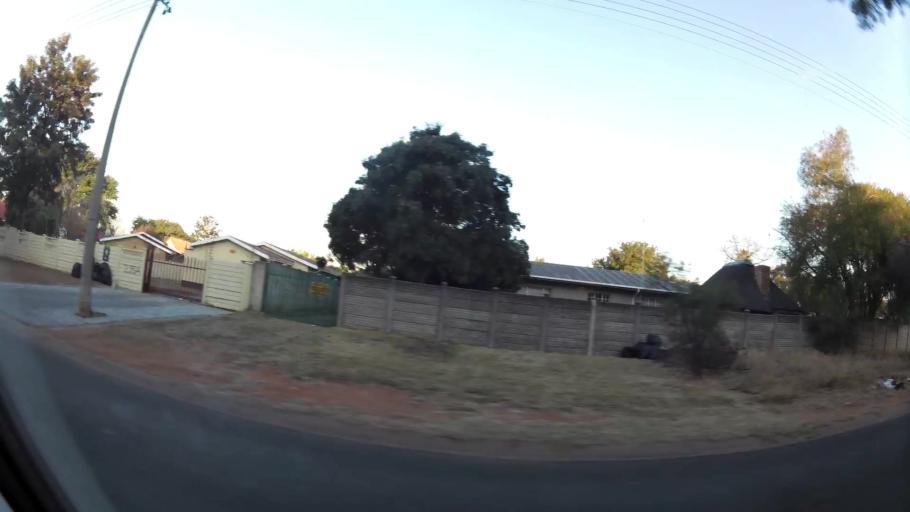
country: ZA
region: North-West
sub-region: Bojanala Platinum District Municipality
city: Rustenburg
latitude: -25.6768
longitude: 27.2210
